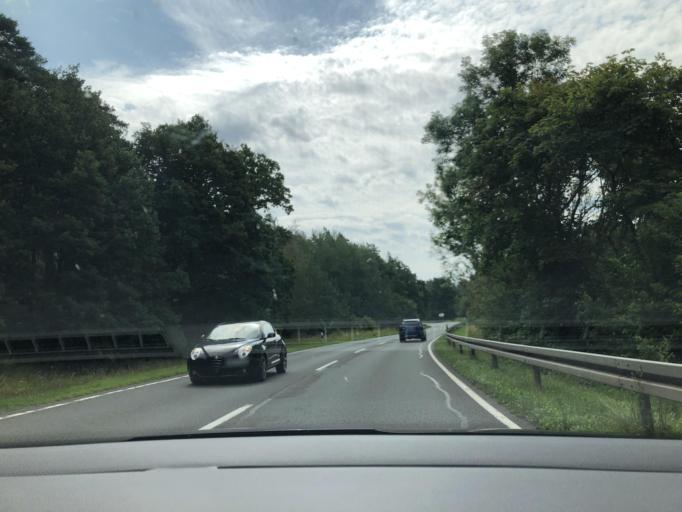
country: DE
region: Saxony-Anhalt
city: Blankenburg
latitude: 51.8191
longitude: 10.9373
